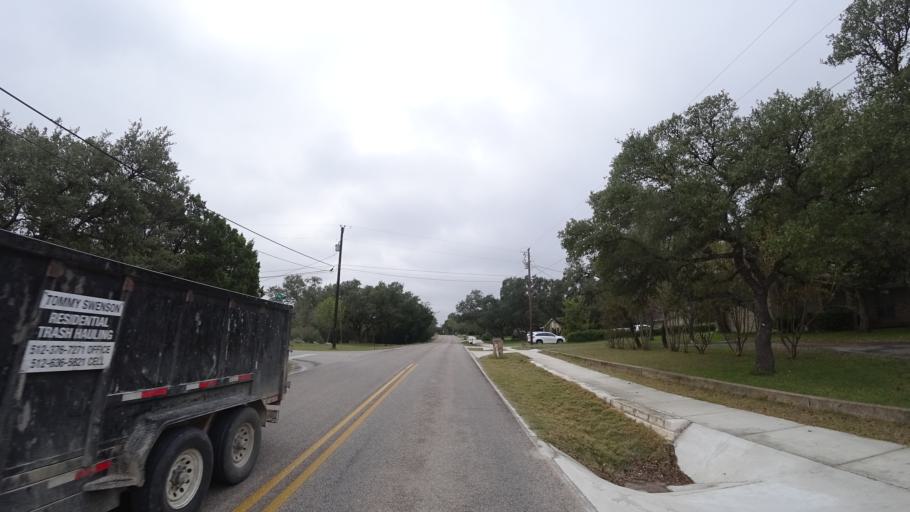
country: US
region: Texas
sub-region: Travis County
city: Barton Creek
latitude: 30.2292
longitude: -97.8962
